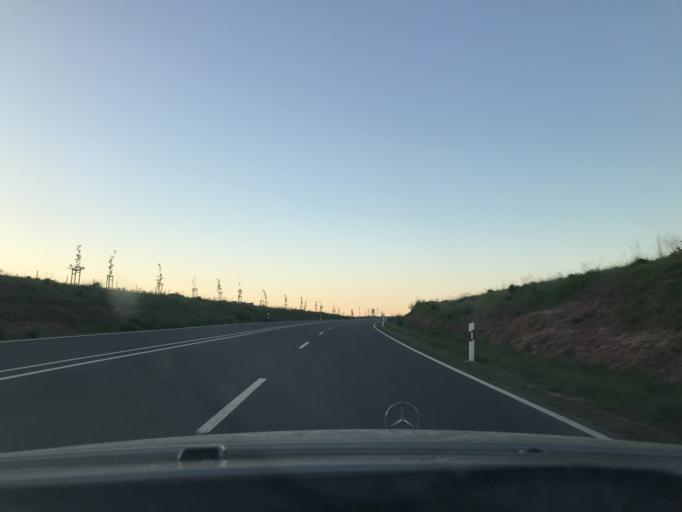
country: DE
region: Thuringia
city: Heilbad Heiligenstadt
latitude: 51.3810
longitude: 10.1142
